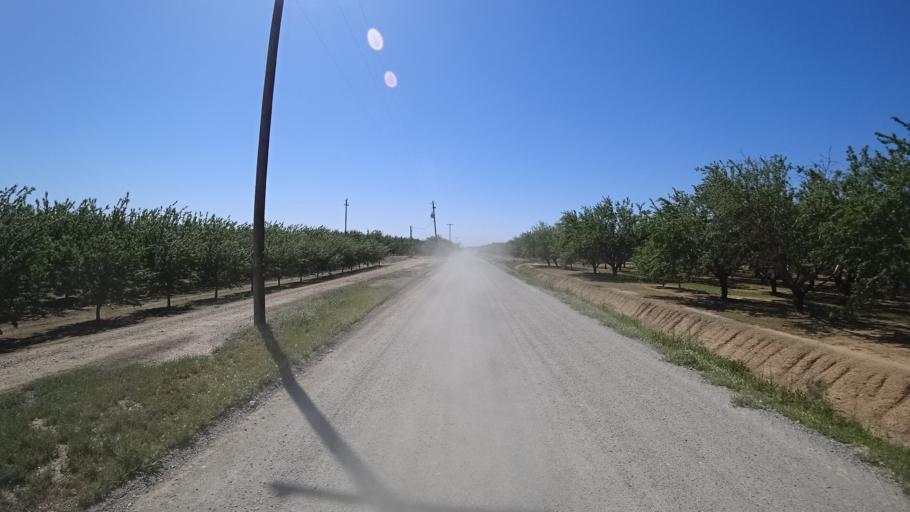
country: US
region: California
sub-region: Glenn County
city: Orland
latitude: 39.6934
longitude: -122.1591
